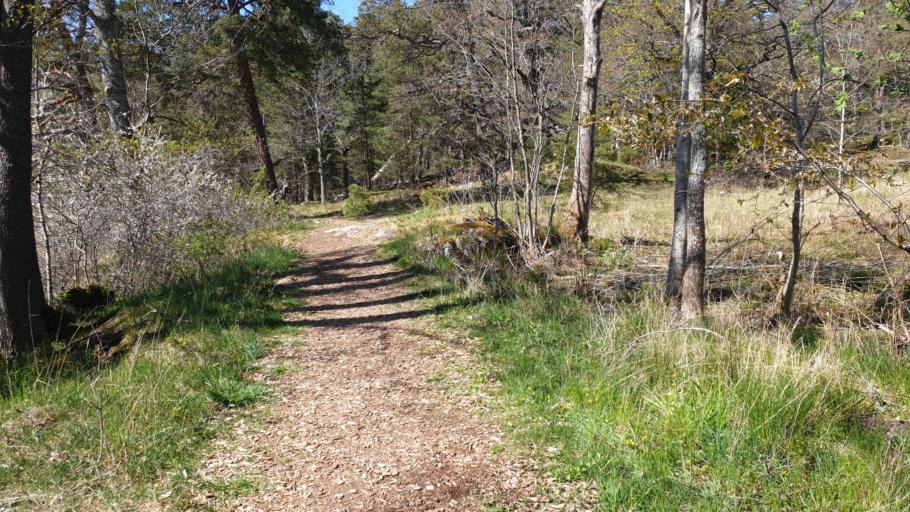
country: SE
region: Stockholm
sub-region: Varmdo Kommun
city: Gustavsberg
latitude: 59.3091
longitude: 18.3501
